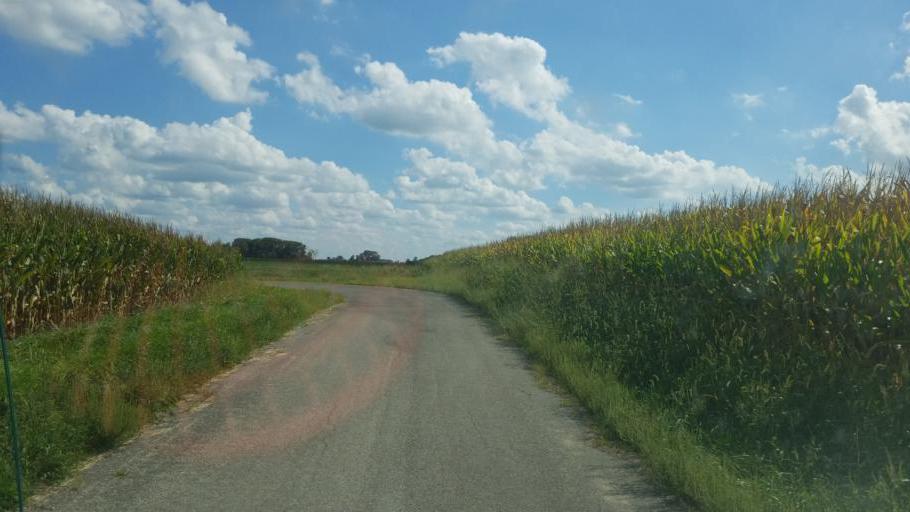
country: US
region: Ohio
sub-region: Union County
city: Richwood
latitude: 40.4657
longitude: -83.3374
